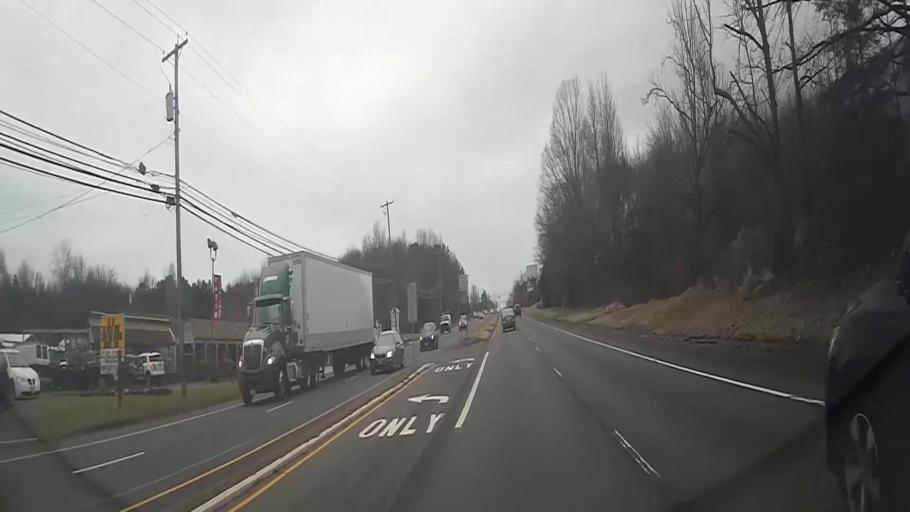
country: US
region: New Jersey
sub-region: Camden County
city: Gibbsboro
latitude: 39.8439
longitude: -74.9240
